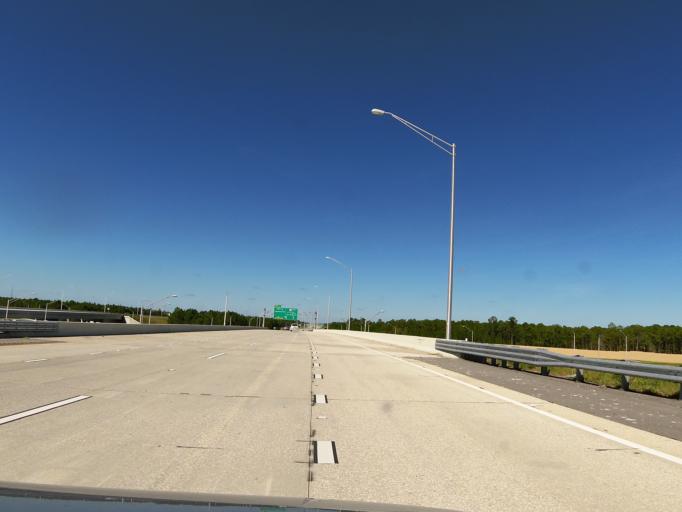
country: US
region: Florida
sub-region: Saint Johns County
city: Fruit Cove
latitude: 30.1128
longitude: -81.5138
